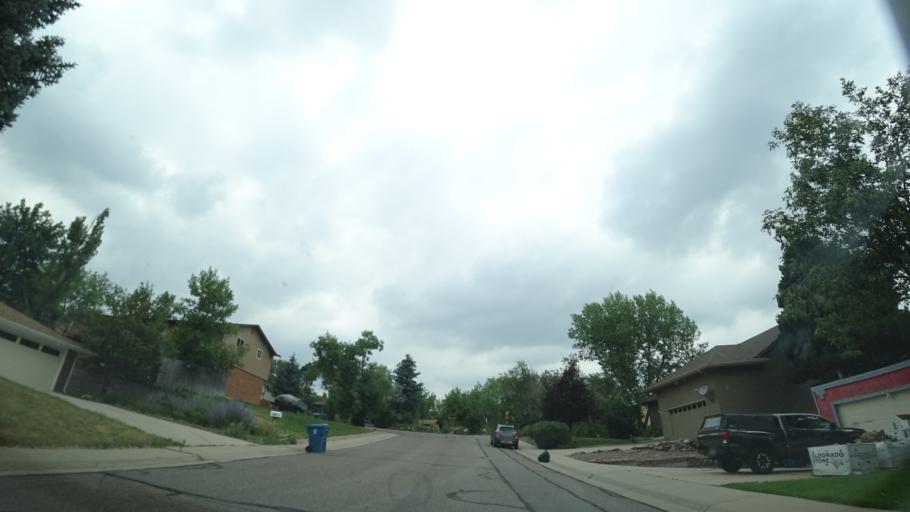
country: US
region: Colorado
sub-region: Jefferson County
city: West Pleasant View
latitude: 39.7097
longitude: -105.1548
